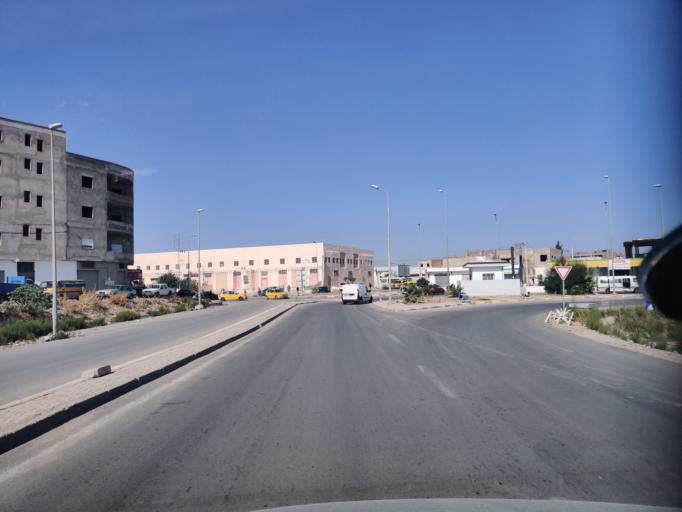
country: TN
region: Manouba
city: Manouba
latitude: 36.7793
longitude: 10.1181
